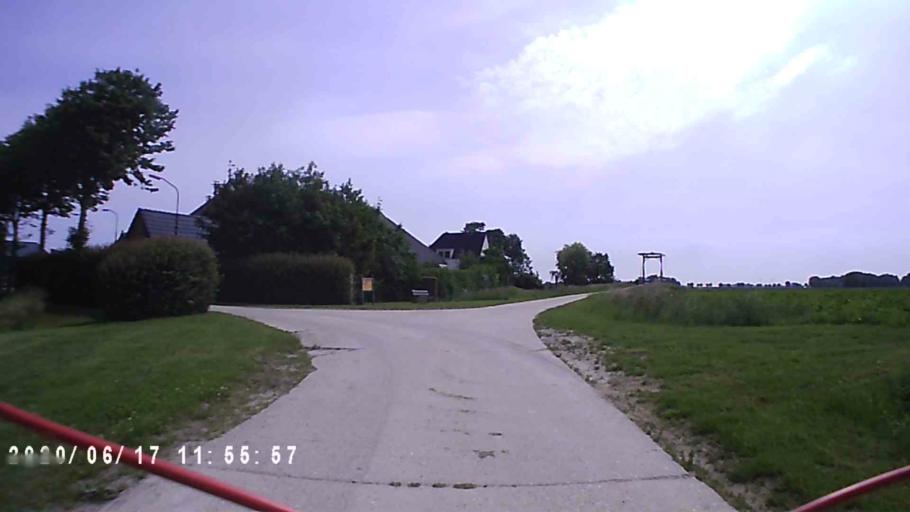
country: NL
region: Groningen
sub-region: Gemeente De Marne
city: Ulrum
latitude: 53.3489
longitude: 6.3189
